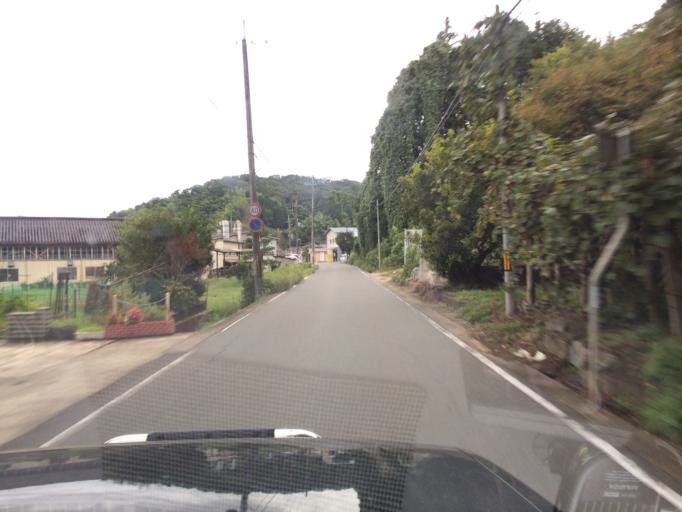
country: JP
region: Hyogo
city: Toyooka
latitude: 35.4882
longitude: 134.7802
